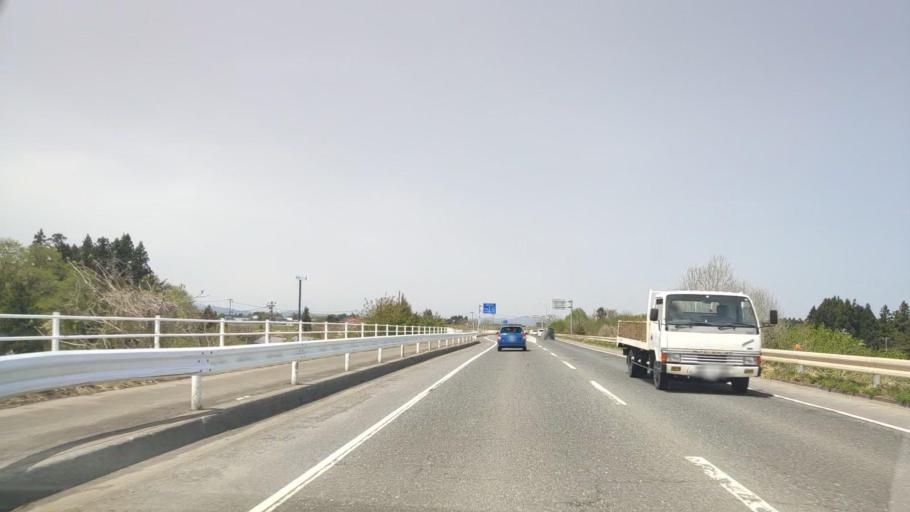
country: JP
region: Aomori
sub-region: Misawa Shi
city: Inuotose
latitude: 40.6317
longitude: 141.2474
